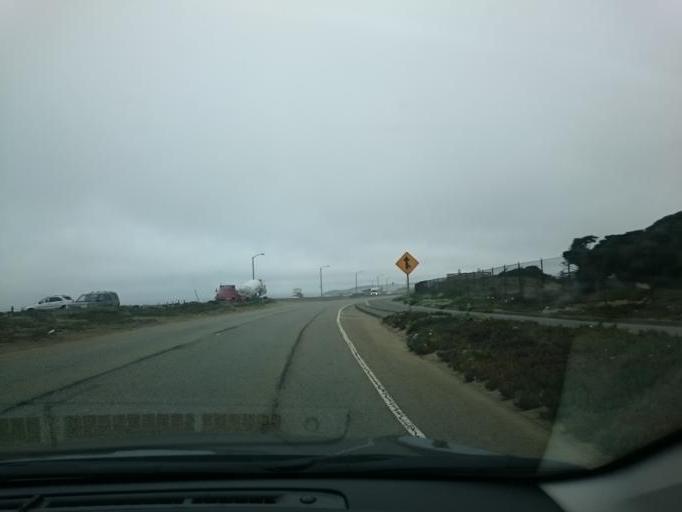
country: US
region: California
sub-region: San Mateo County
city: Broadmoor
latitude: 37.7326
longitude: -122.5070
